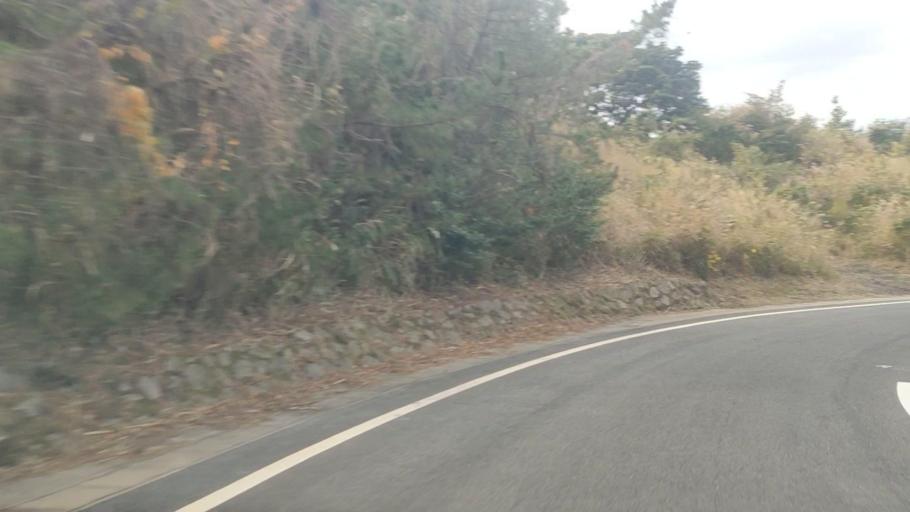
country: JP
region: Kagoshima
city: Kagoshima-shi
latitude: 31.5754
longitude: 130.6202
